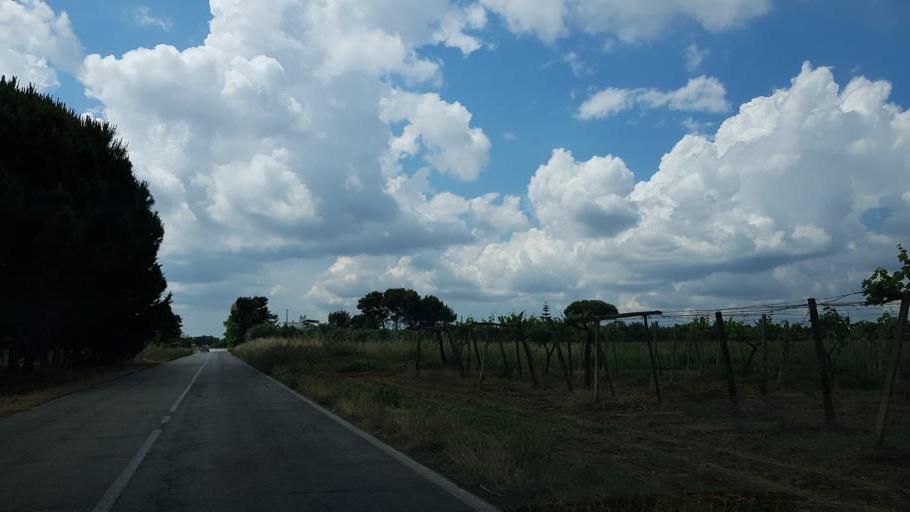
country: IT
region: Apulia
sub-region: Provincia di Brindisi
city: Mesagne
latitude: 40.5363
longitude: 17.8183
